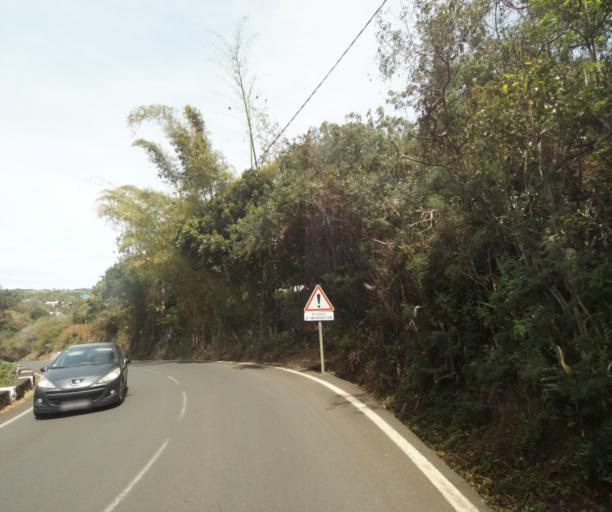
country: RE
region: Reunion
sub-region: Reunion
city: Saint-Paul
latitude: -21.0462
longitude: 55.2873
